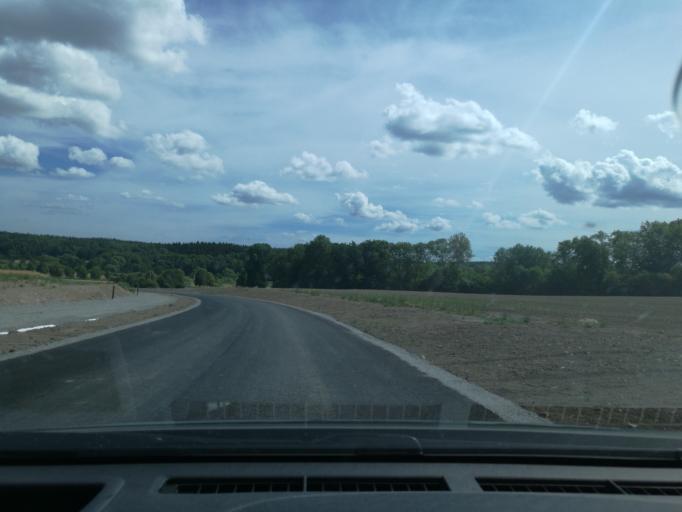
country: SE
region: Stockholm
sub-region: Sigtuna Kommun
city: Marsta
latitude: 59.6052
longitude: 17.8054
